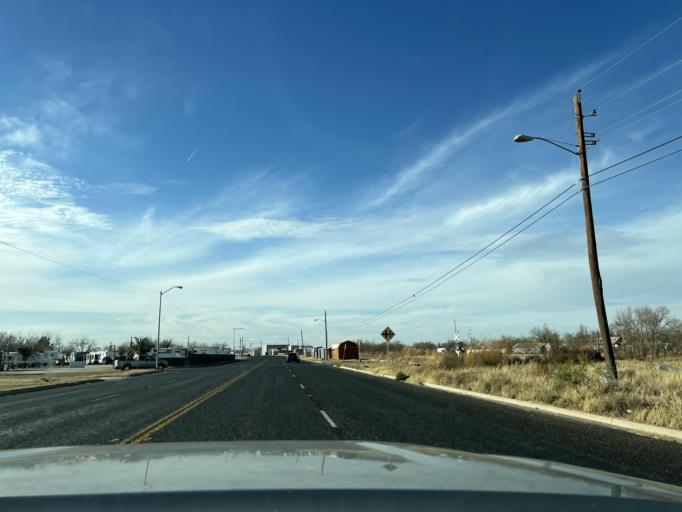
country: US
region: Texas
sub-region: Scurry County
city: Snyder
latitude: 32.7133
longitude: -100.8947
